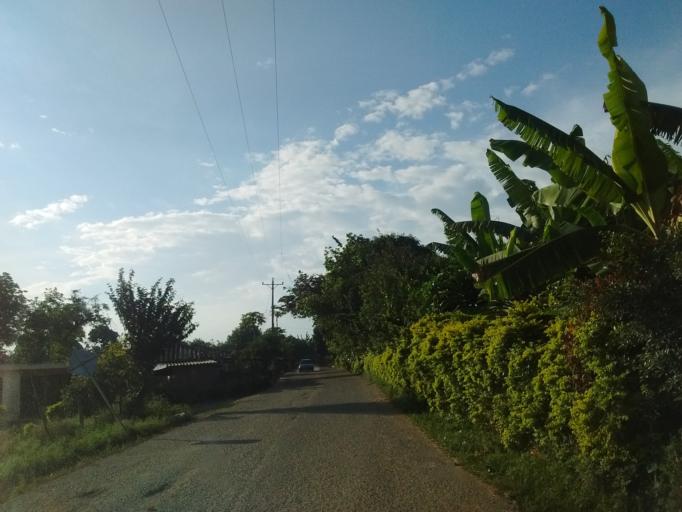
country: CO
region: Cauca
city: Puerto Tejada
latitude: 3.2146
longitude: -76.4450
